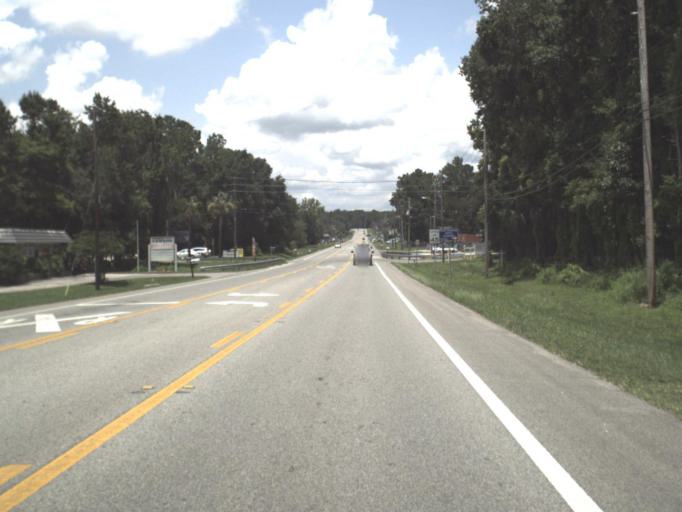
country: US
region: Florida
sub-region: Hernando County
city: Brooksville
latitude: 28.5623
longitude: -82.3976
